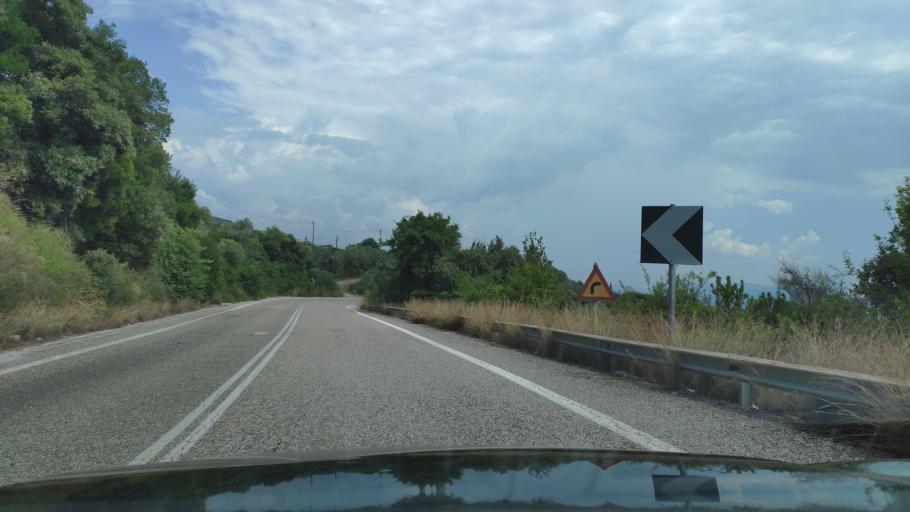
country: GR
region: West Greece
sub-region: Nomos Aitolias kai Akarnanias
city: Menidi
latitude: 39.0005
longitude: 21.1496
